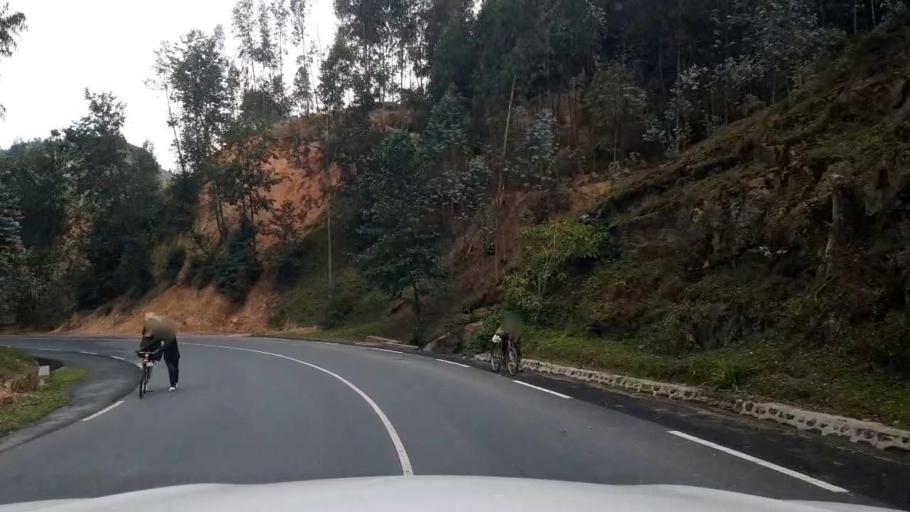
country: RW
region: Northern Province
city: Musanze
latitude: -1.6866
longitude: 29.5241
